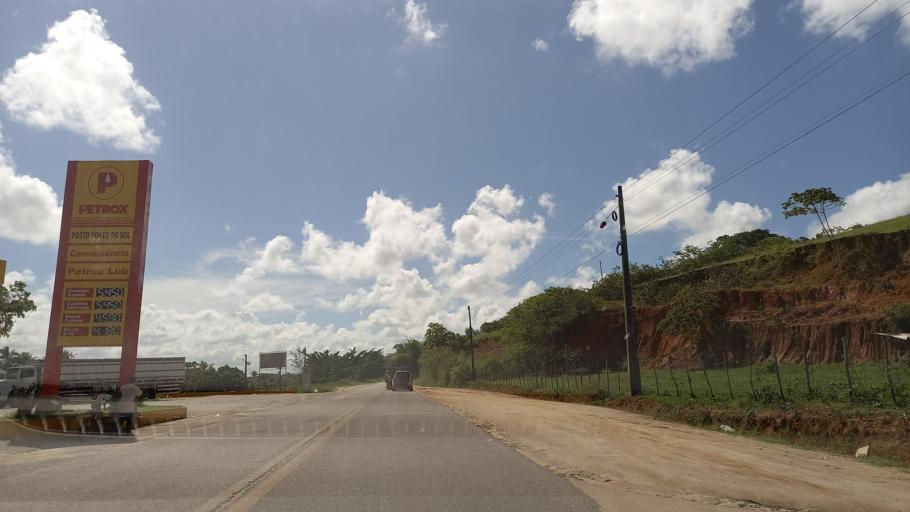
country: BR
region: Pernambuco
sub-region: Barreiros
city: Barreiros
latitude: -8.8039
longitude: -35.1876
